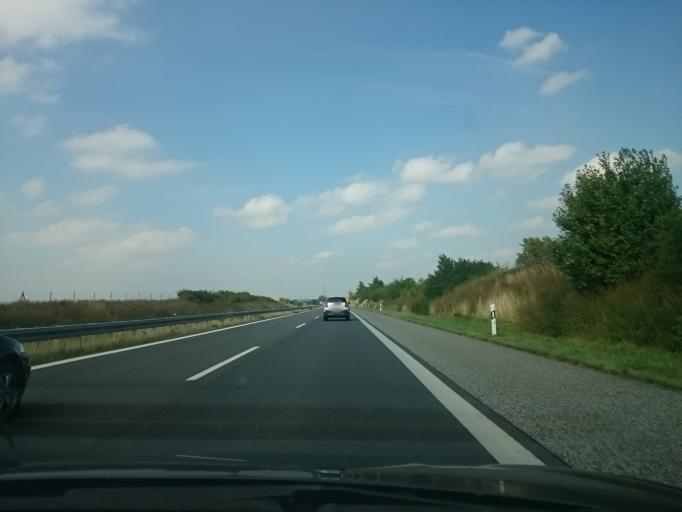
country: DE
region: Brandenburg
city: Schonfeld
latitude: 53.4293
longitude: 13.9966
